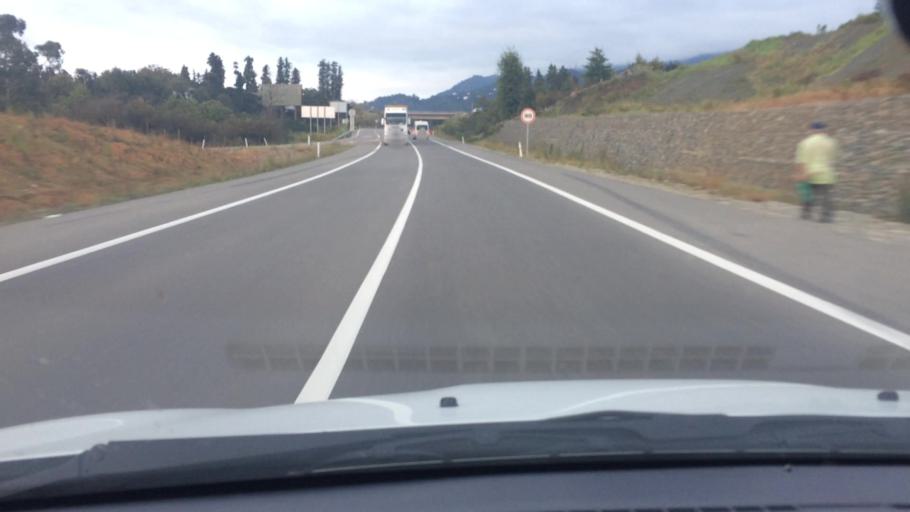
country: GE
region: Ajaria
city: Makhinjauri
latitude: 41.7042
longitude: 41.7383
